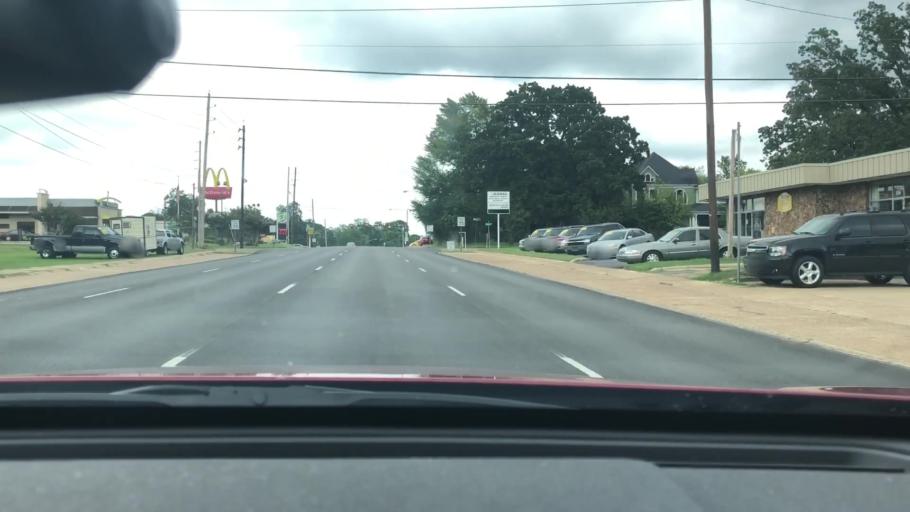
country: US
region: Texas
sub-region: Bowie County
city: Texarkana
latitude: 33.4296
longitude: -94.0380
